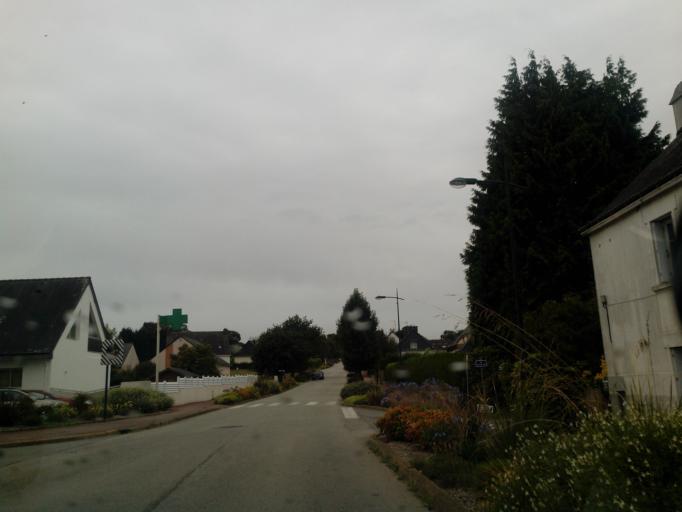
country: FR
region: Brittany
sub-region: Departement du Finistere
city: Tremeven
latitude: 47.9004
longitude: -3.5219
